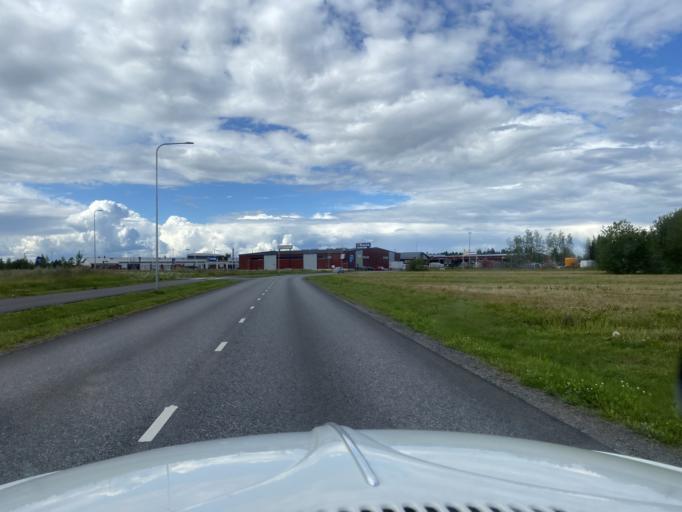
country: FI
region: Satakunta
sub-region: Pori
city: Huittinen
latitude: 61.1708
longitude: 22.6834
